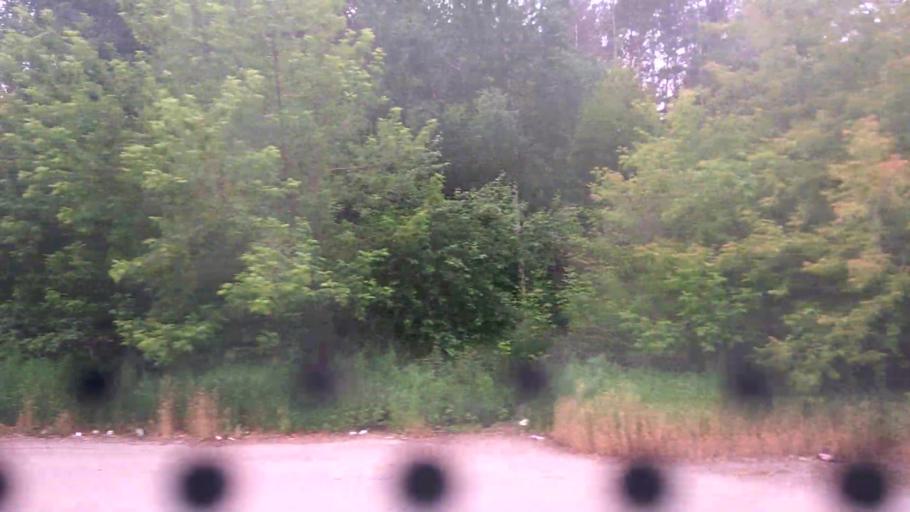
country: RU
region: Moskovskaya
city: Kolomna
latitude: 55.0556
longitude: 38.8648
